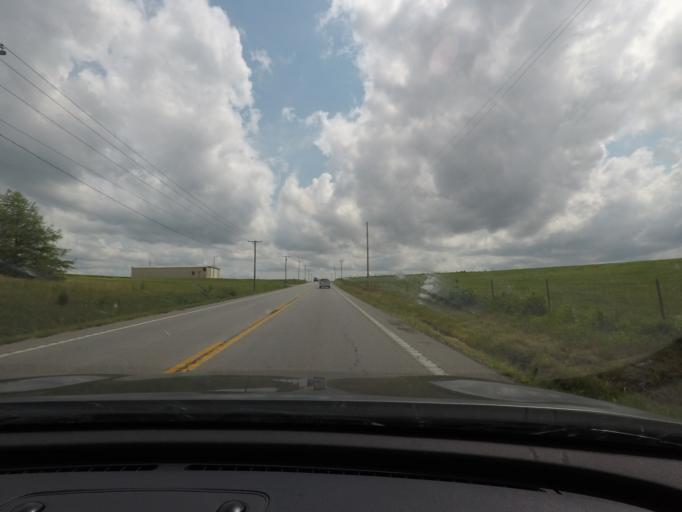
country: US
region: Missouri
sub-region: Lafayette County
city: Higginsville
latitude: 39.0275
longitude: -93.7343
